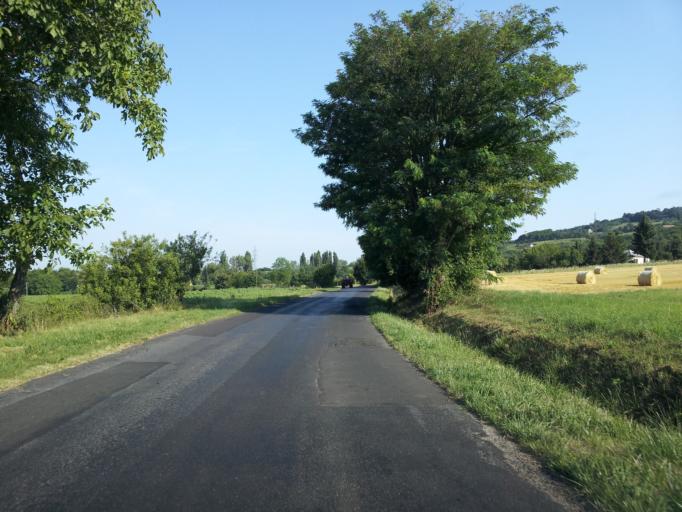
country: HU
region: Zala
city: Gyenesdias
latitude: 46.8555
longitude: 17.3262
